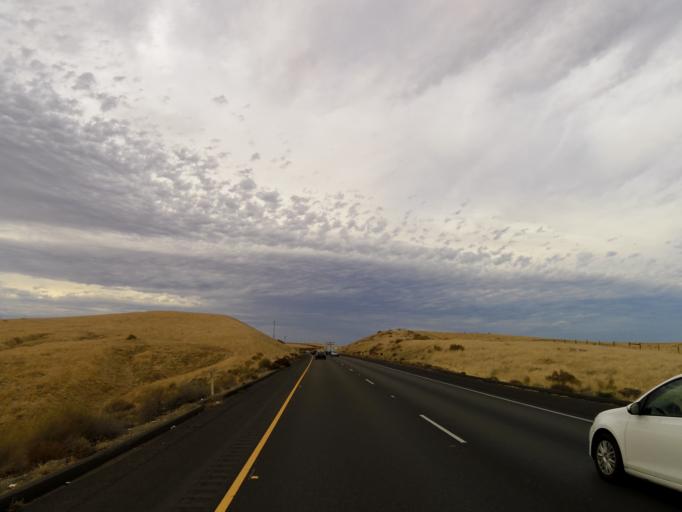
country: US
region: California
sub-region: Kings County
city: Kettleman City
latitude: 36.0027
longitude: -119.9803
